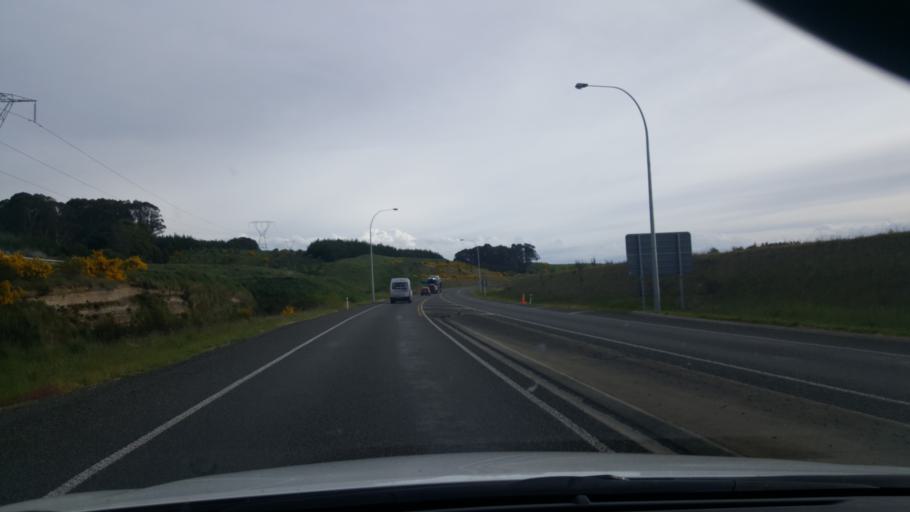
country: NZ
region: Waikato
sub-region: Taupo District
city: Taupo
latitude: -38.7062
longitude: 176.1120
